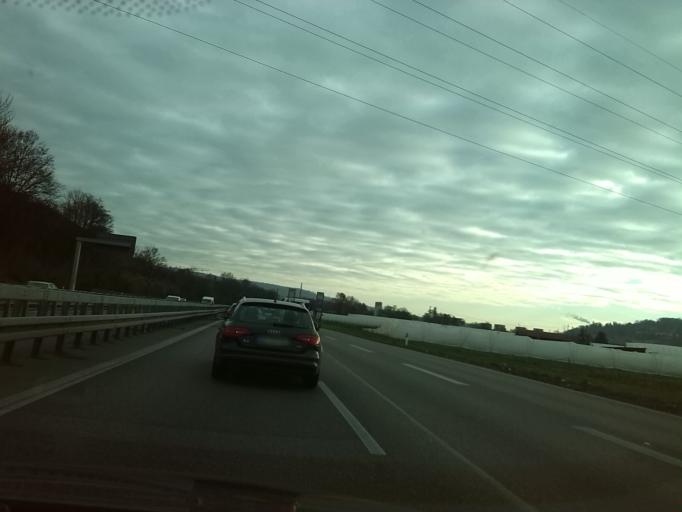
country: DE
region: Baden-Wuerttemberg
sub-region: Regierungsbezirk Stuttgart
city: Esslingen
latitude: 48.7404
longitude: 9.2782
